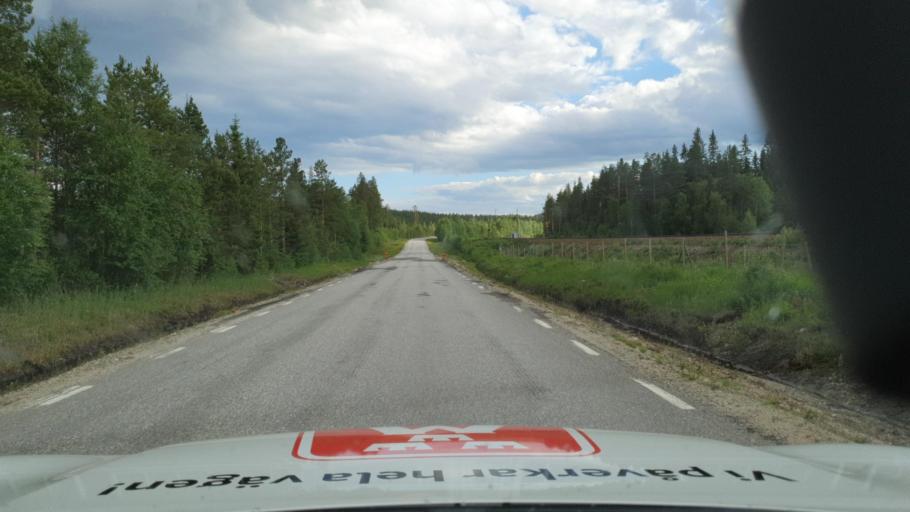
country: SE
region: Vaesterbotten
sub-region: Vindelns Kommun
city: Vindeln
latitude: 64.3635
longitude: 19.6566
